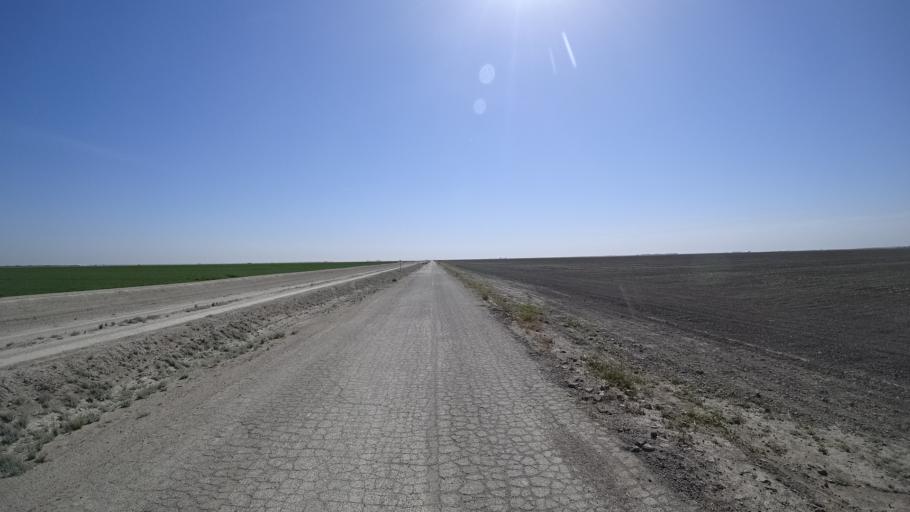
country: US
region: California
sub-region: Kings County
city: Corcoran
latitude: 35.9781
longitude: -119.5705
